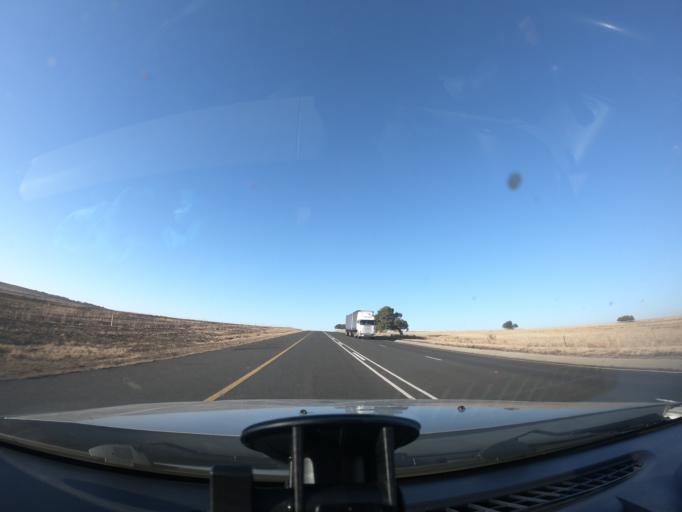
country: ZA
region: Mpumalanga
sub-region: Gert Sibande District Municipality
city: Ermelo
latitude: -26.4520
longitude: 29.9500
